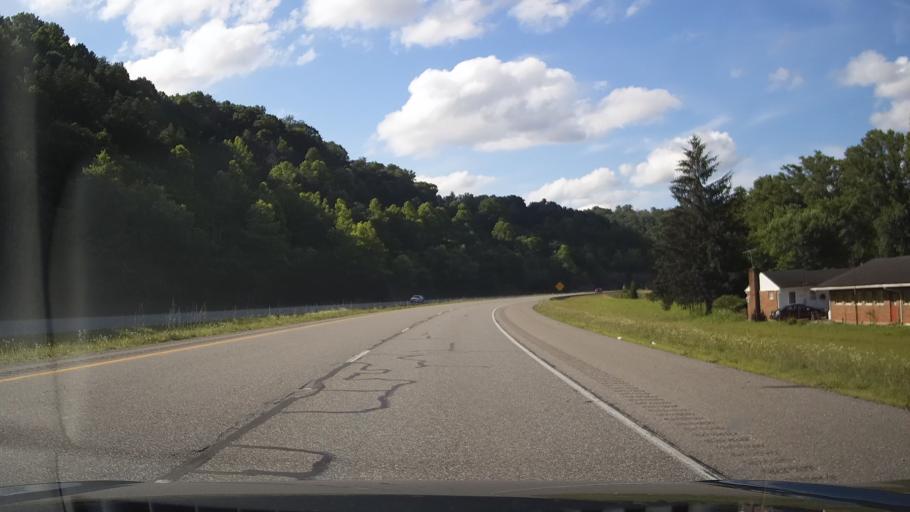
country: US
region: Kentucky
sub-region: Lawrence County
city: Louisa
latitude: 38.1630
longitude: -82.6451
